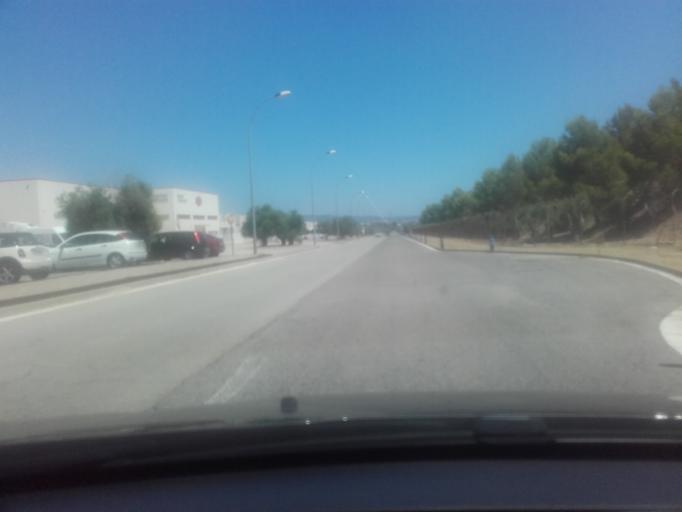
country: ES
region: Catalonia
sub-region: Provincia de Tarragona
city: Santa Oliva
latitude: 41.2691
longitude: 1.5174
